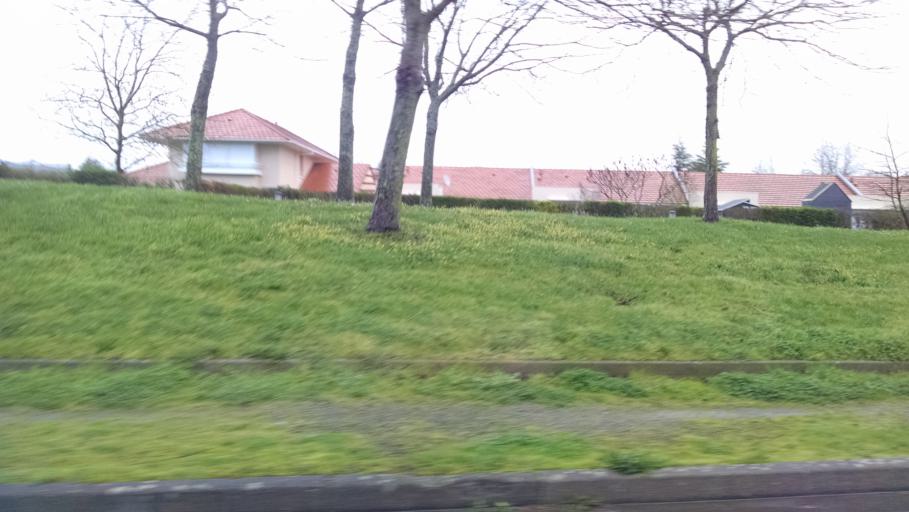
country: FR
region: Pays de la Loire
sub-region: Departement de la Loire-Atlantique
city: Aigrefeuille-sur-Maine
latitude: 47.0810
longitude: -1.4023
